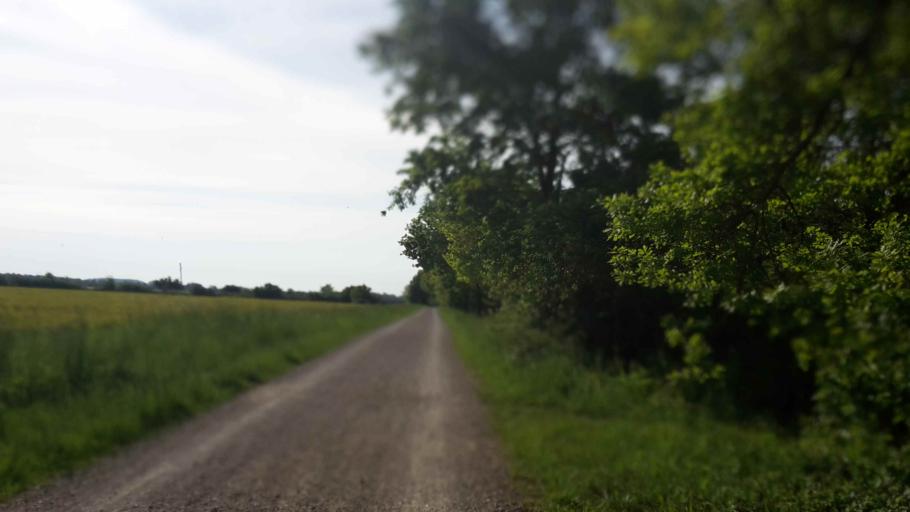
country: DE
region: Bavaria
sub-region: Upper Bavaria
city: Garching bei Munchen
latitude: 48.2420
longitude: 11.6252
